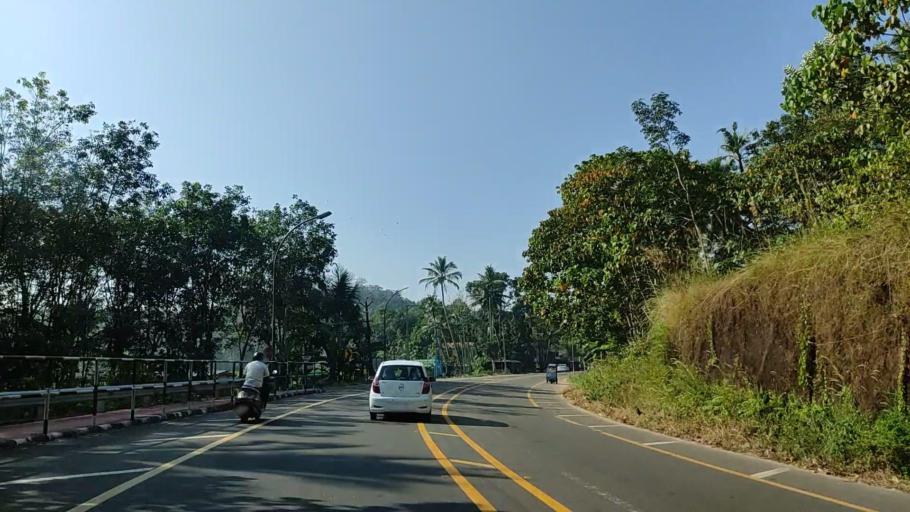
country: IN
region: Kerala
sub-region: Kollam
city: Punalur
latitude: 8.9188
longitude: 76.8552
